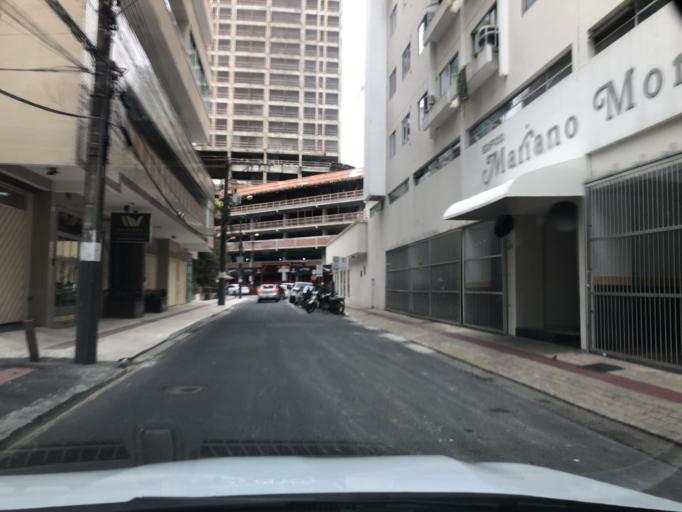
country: BR
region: Santa Catarina
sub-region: Balneario Camboriu
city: Balneario Camboriu
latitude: -27.0009
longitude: -48.6234
